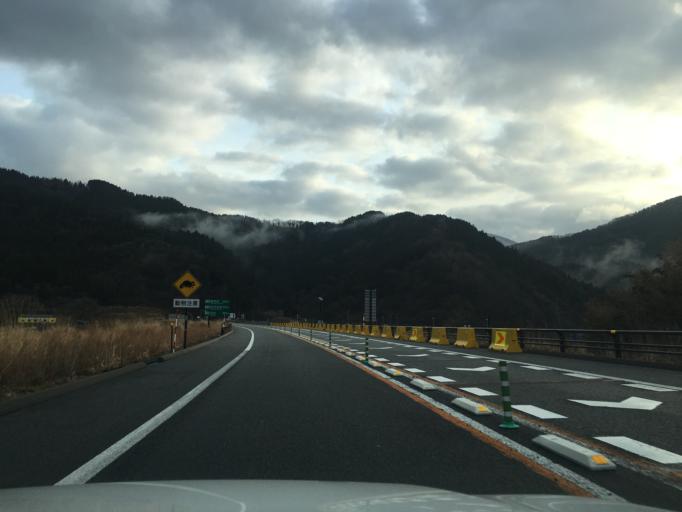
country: JP
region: Yamagata
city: Tsuruoka
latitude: 38.6037
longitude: 139.5846
